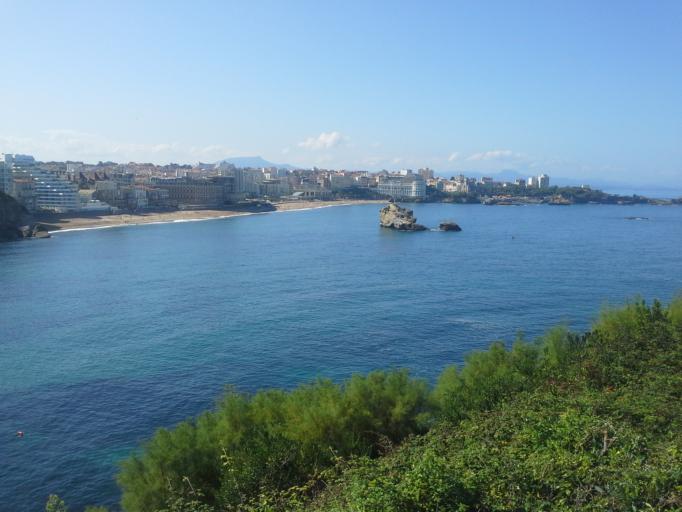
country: FR
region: Aquitaine
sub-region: Departement des Pyrenees-Atlantiques
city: Biarritz
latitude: 43.4932
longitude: -1.5541
